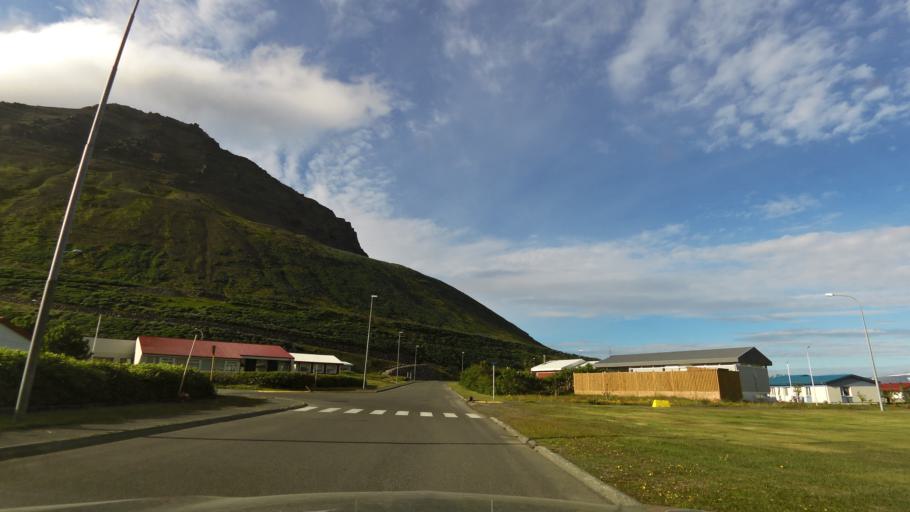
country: IS
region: Westfjords
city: Isafjoerdur
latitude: 66.1595
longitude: -23.2623
